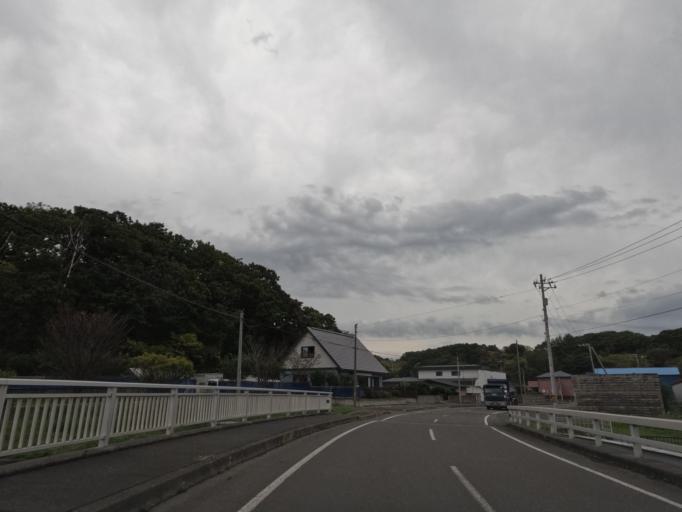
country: JP
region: Hokkaido
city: Date
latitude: 42.3940
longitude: 140.9087
